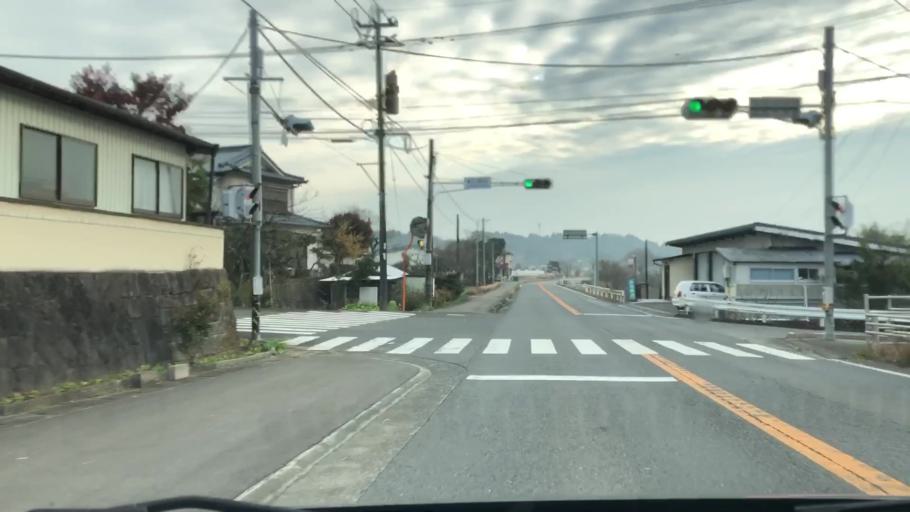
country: JP
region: Oita
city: Takedamachi
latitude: 32.9695
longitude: 131.4683
